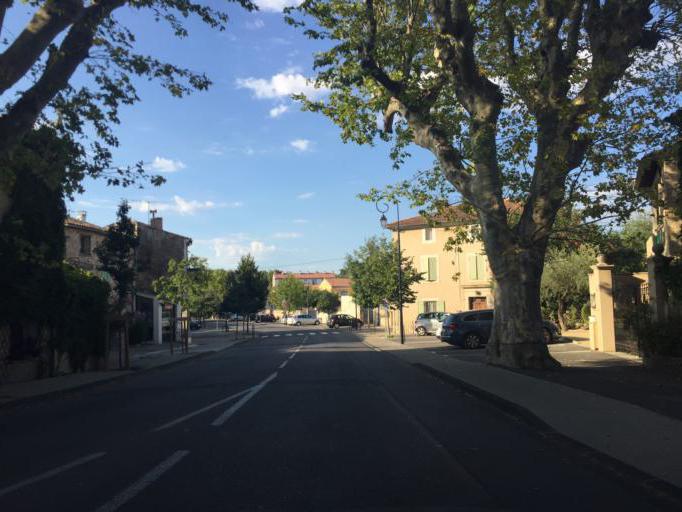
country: FR
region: Provence-Alpes-Cote d'Azur
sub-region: Departement du Vaucluse
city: Pernes-les-Fontaines
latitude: 43.9974
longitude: 5.0622
